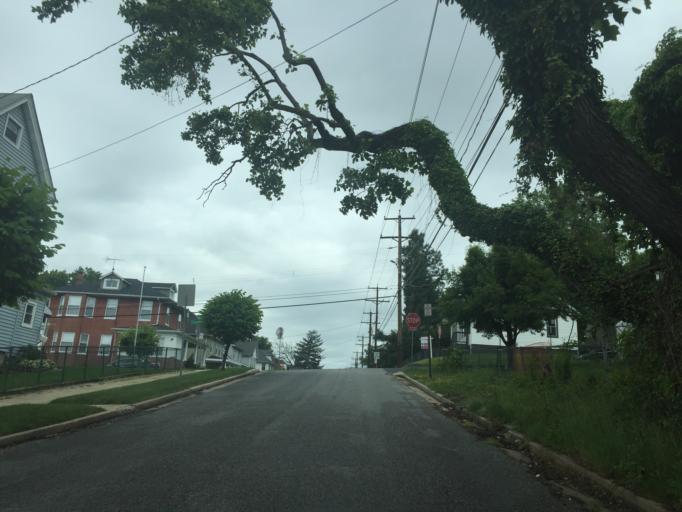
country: US
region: Maryland
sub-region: Baltimore County
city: Overlea
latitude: 39.3547
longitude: -76.5265
